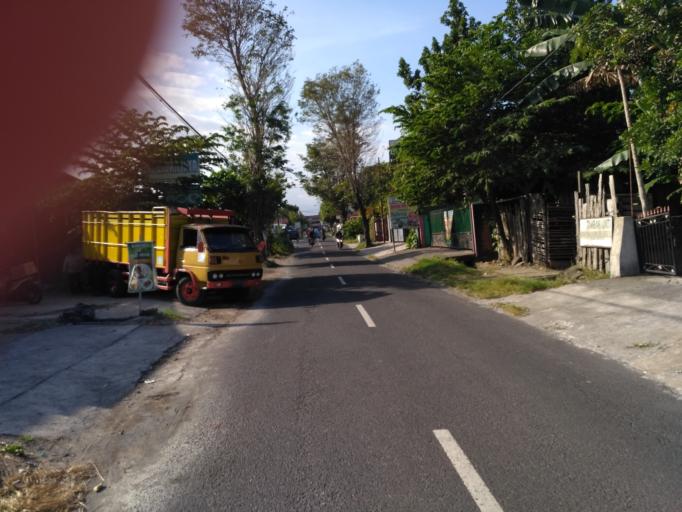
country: ID
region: Daerah Istimewa Yogyakarta
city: Depok
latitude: -7.7761
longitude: 110.4235
